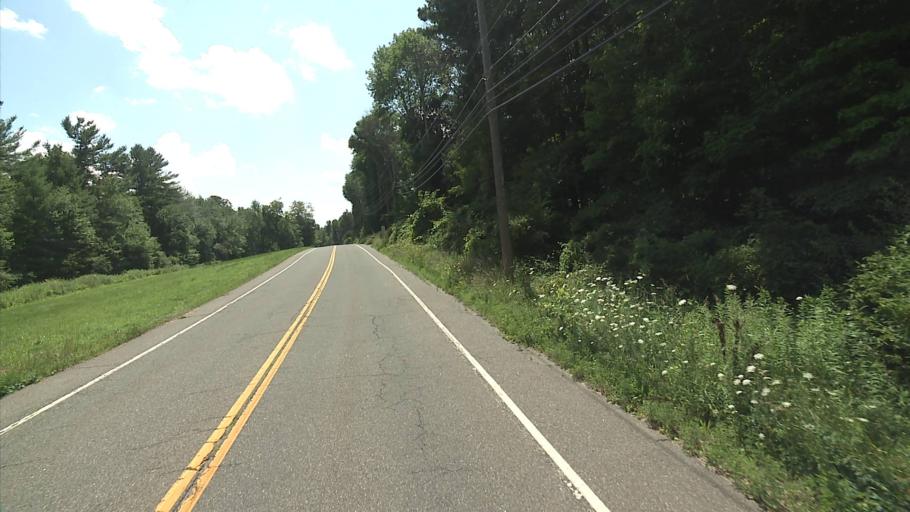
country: US
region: Connecticut
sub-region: Litchfield County
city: Canaan
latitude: 41.8671
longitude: -73.3301
